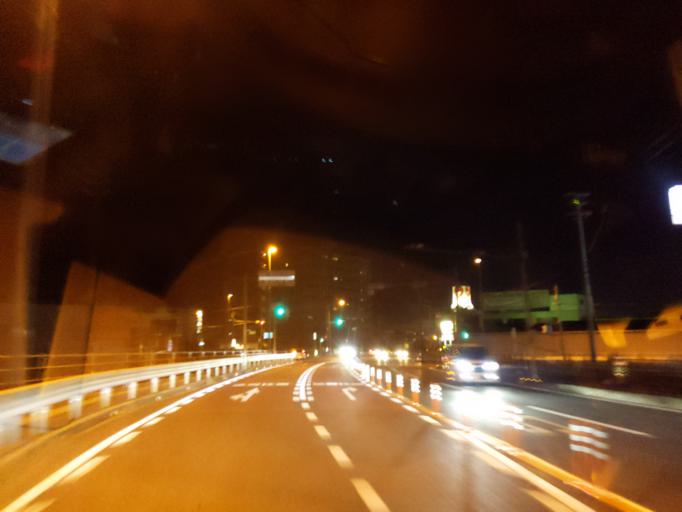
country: JP
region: Okayama
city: Okayama-shi
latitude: 34.6723
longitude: 133.9571
